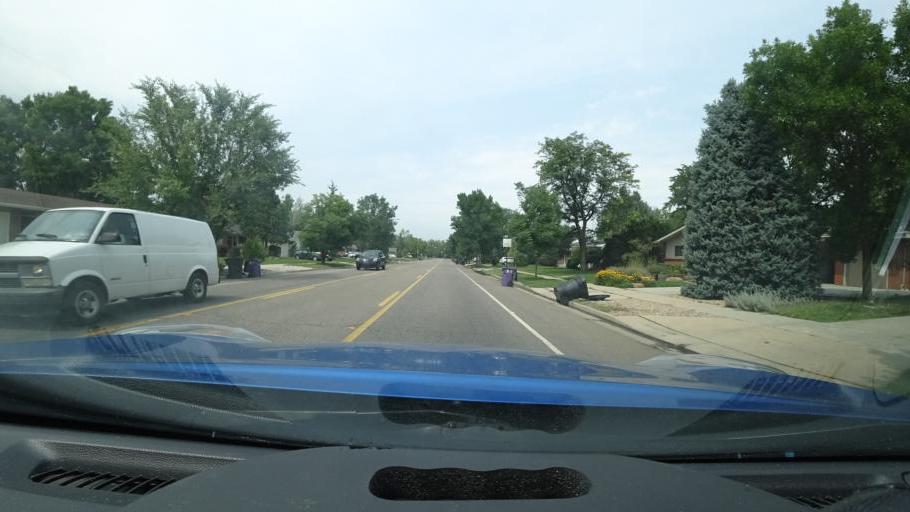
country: US
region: Colorado
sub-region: Arapahoe County
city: Glendale
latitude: 39.7017
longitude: -104.9216
